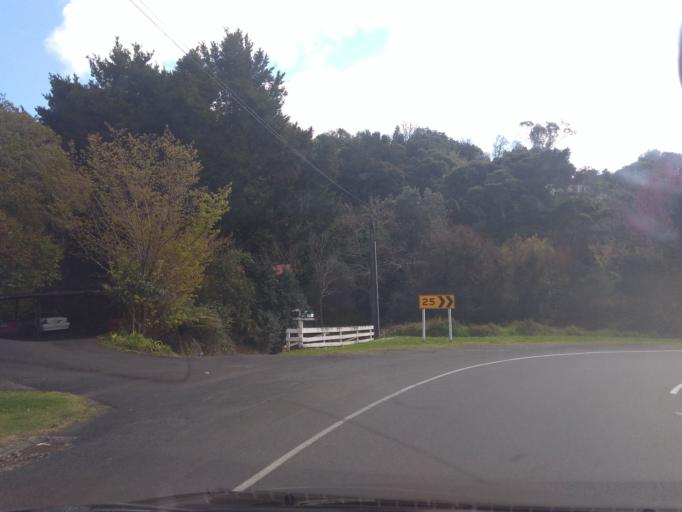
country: NZ
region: Northland
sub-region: Whangarei
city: Whangarei
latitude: -35.7021
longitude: 174.3291
